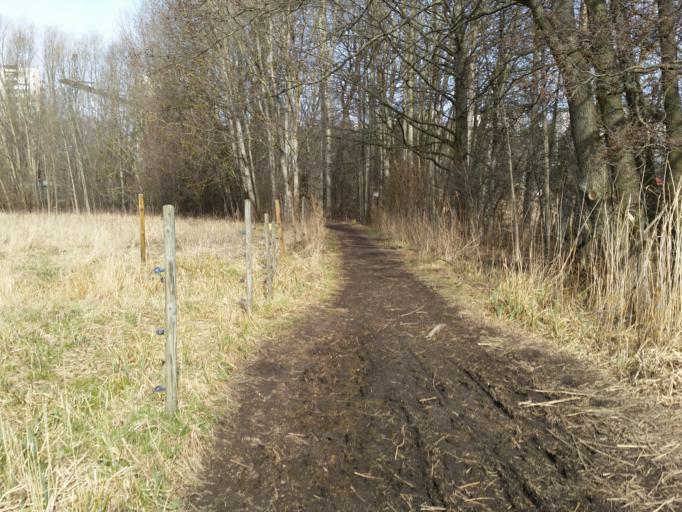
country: SE
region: Stockholm
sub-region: Norrtalje Kommun
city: Bergshamra
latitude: 59.3749
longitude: 18.0422
